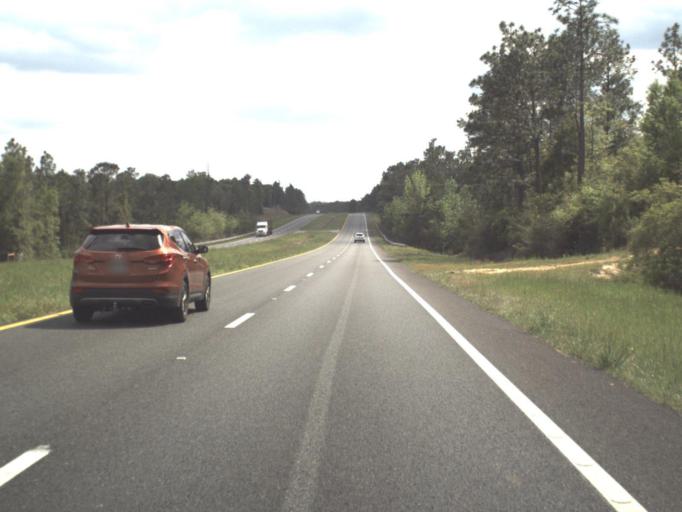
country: US
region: Florida
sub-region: Escambia County
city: Molino
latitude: 30.8352
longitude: -87.3290
